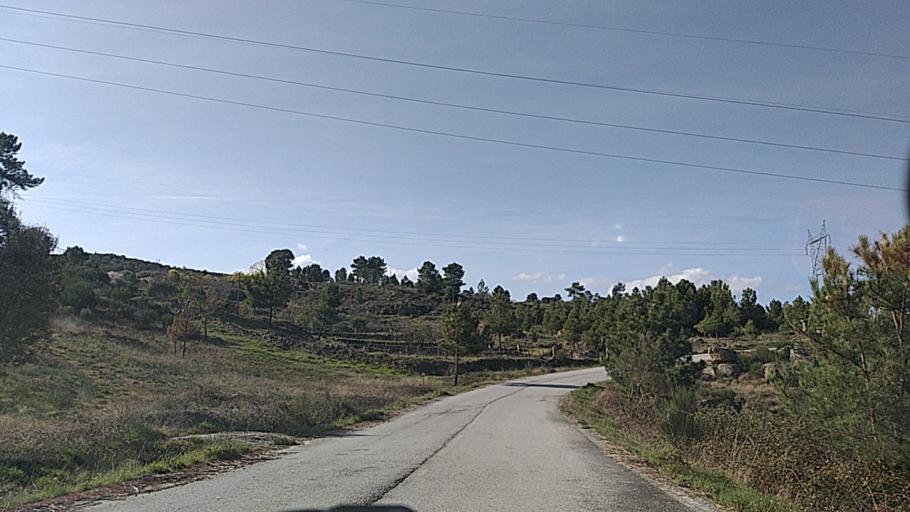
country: PT
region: Guarda
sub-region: Celorico da Beira
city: Celorico da Beira
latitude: 40.6526
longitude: -7.3980
